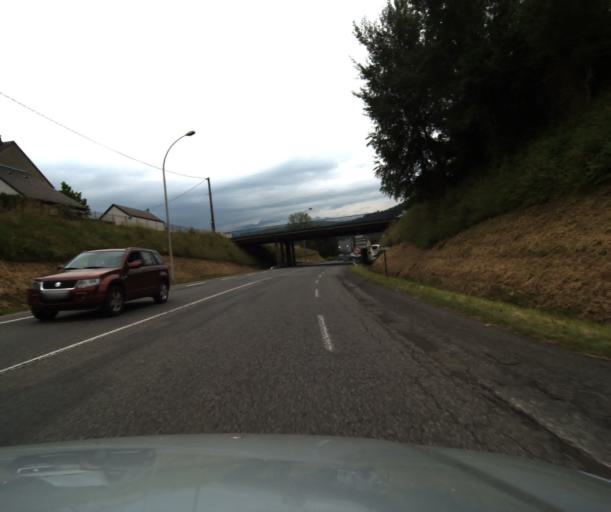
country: FR
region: Midi-Pyrenees
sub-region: Departement des Hautes-Pyrenees
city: Lourdes
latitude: 43.1030
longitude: -0.0302
